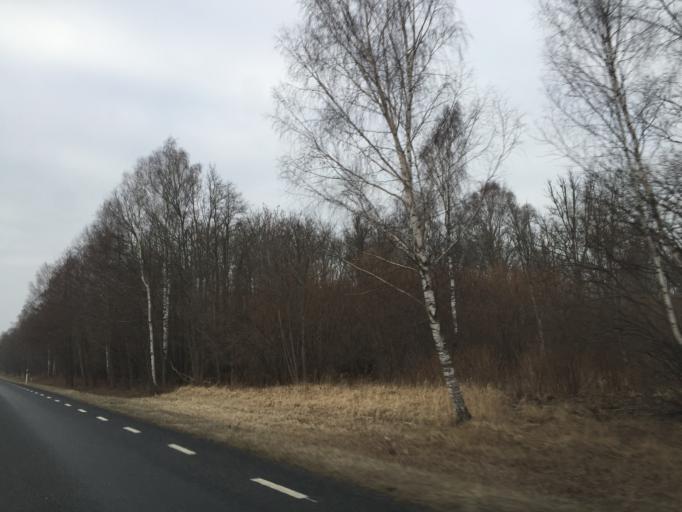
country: EE
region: Saare
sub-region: Orissaare vald
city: Orissaare
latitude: 58.6045
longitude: 23.3016
